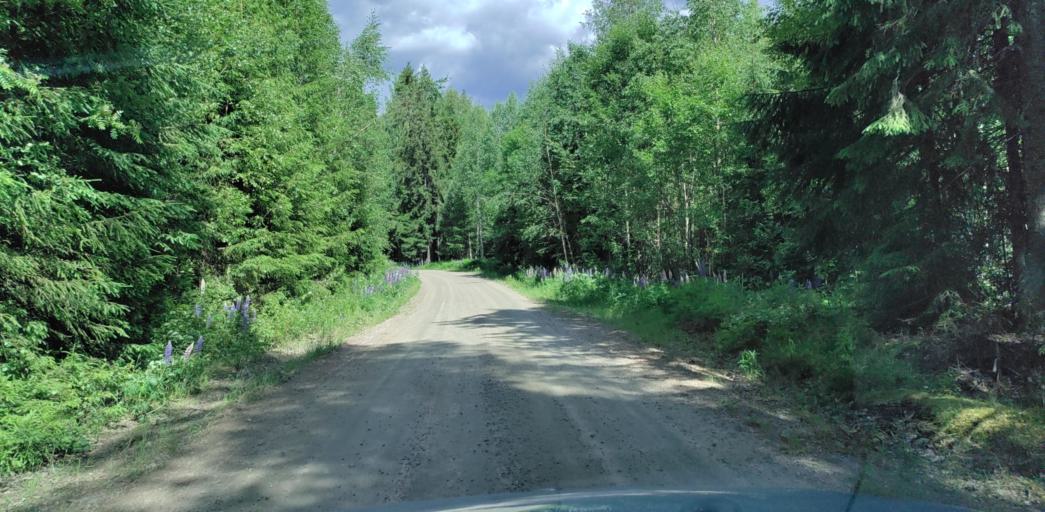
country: SE
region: Vaermland
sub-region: Sunne Kommun
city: Sunne
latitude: 60.0408
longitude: 13.2509
